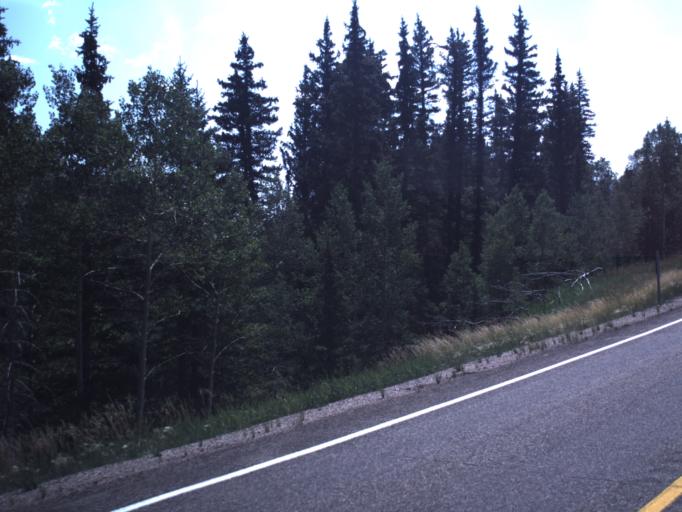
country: US
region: Utah
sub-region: Uintah County
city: Maeser
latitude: 40.7068
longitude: -109.4943
